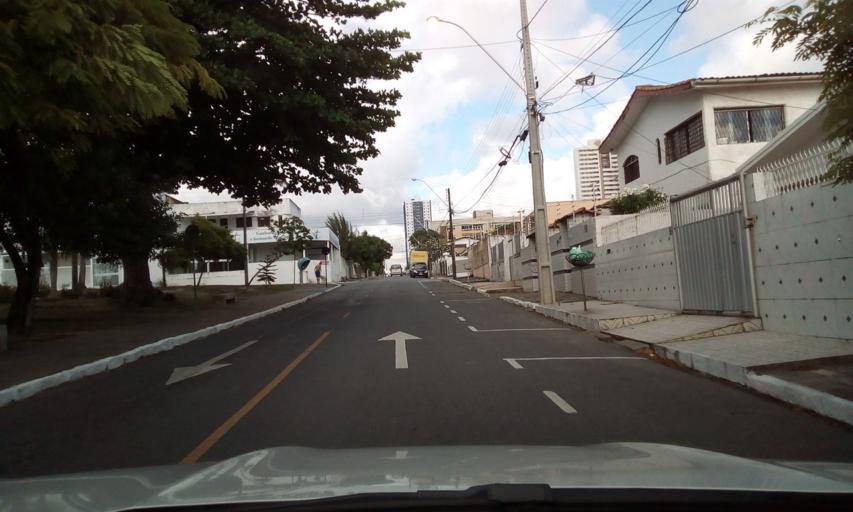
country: BR
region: Paraiba
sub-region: Joao Pessoa
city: Joao Pessoa
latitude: -7.1155
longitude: -34.8477
